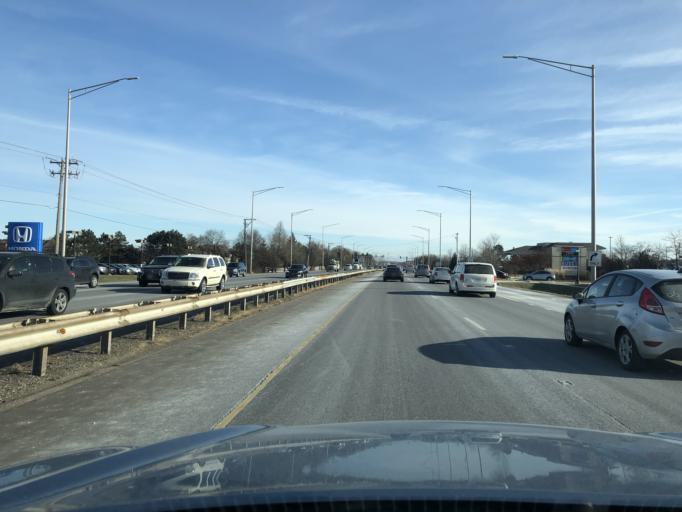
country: US
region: Illinois
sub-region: Lake County
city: Grandwood Park
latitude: 42.3859
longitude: -87.9757
